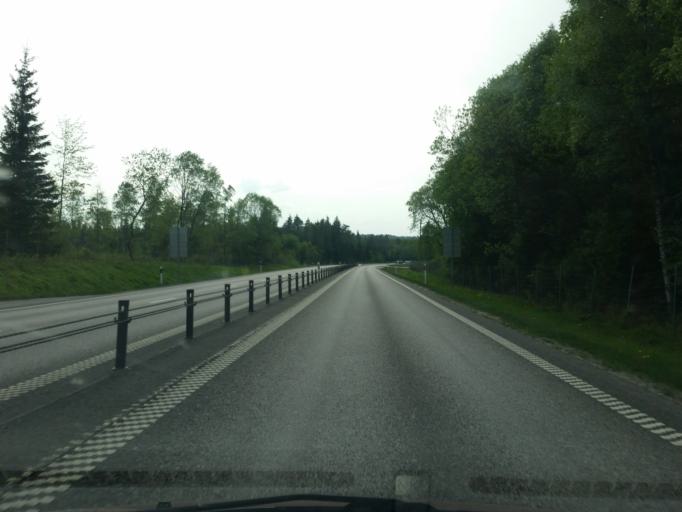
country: SE
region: Vaestra Goetaland
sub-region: Ulricehamns Kommun
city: Ulricehamn
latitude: 57.7958
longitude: 13.5573
